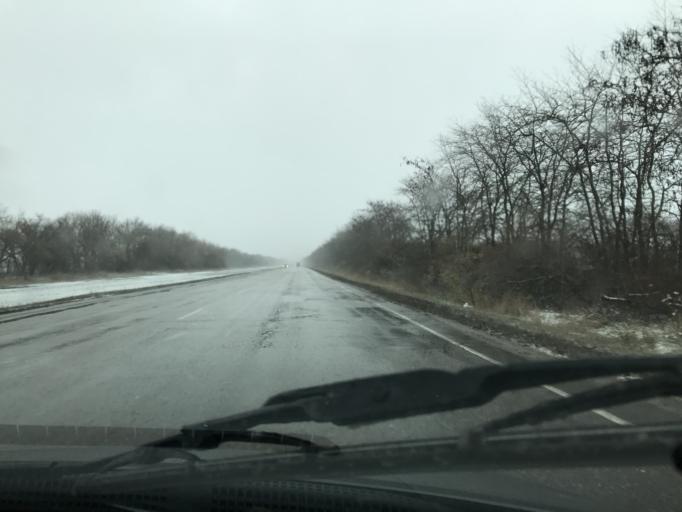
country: RU
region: Rostov
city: Kirovskaya
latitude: 47.0050
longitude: 39.9617
